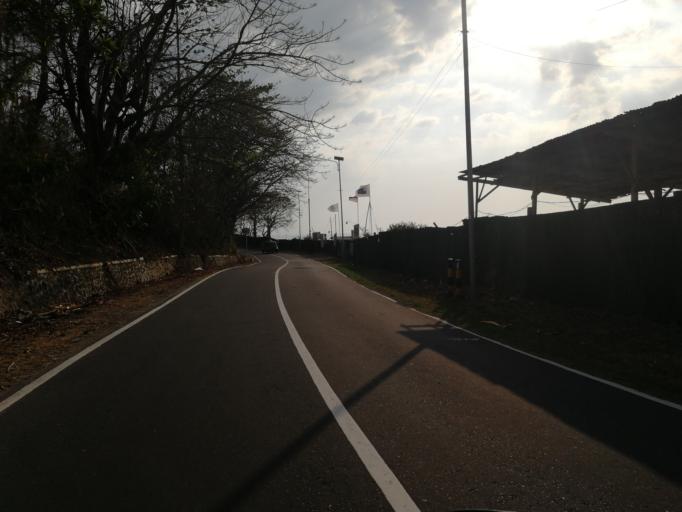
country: ID
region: West Nusa Tenggara
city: Karangsubagan
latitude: -8.4464
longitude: 116.0340
